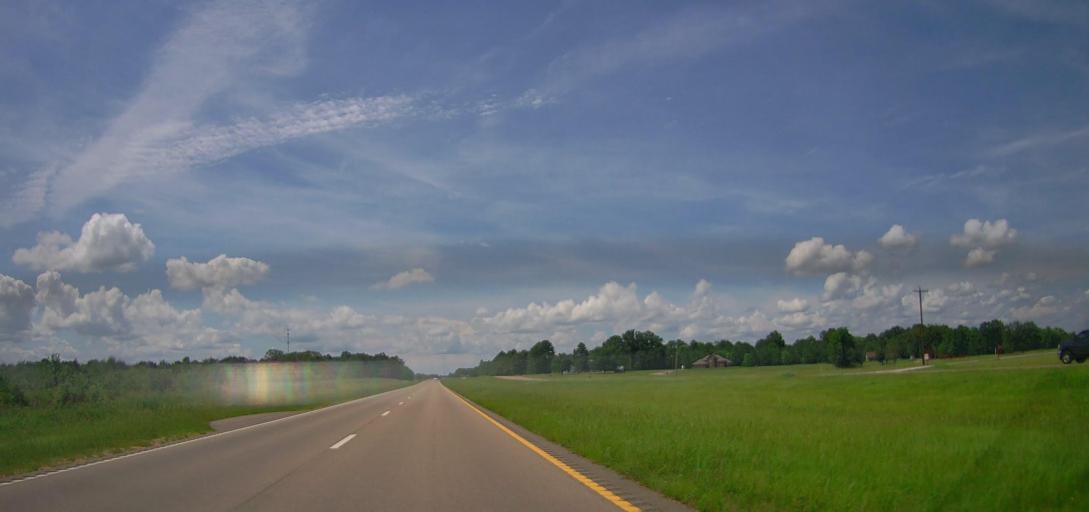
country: US
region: Mississippi
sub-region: Lee County
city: Nettleton
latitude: 33.9799
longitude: -88.6162
